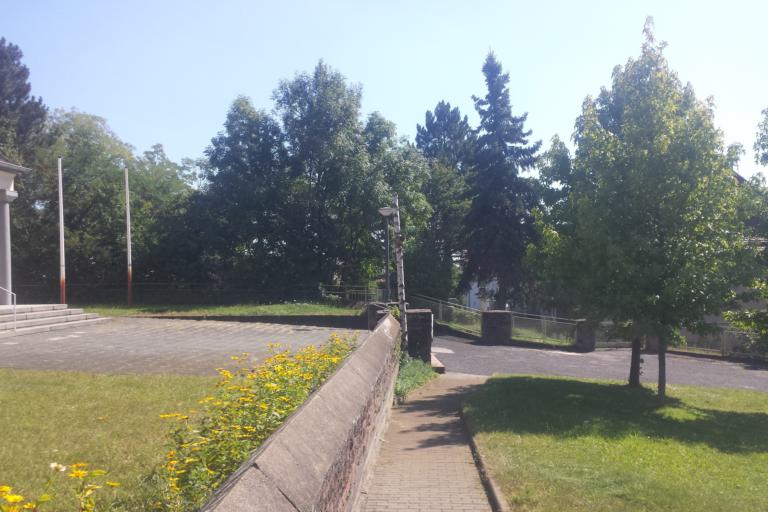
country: DE
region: Baden-Wuerttemberg
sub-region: Karlsruhe Region
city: Mannheim
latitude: 49.5246
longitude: 8.5073
